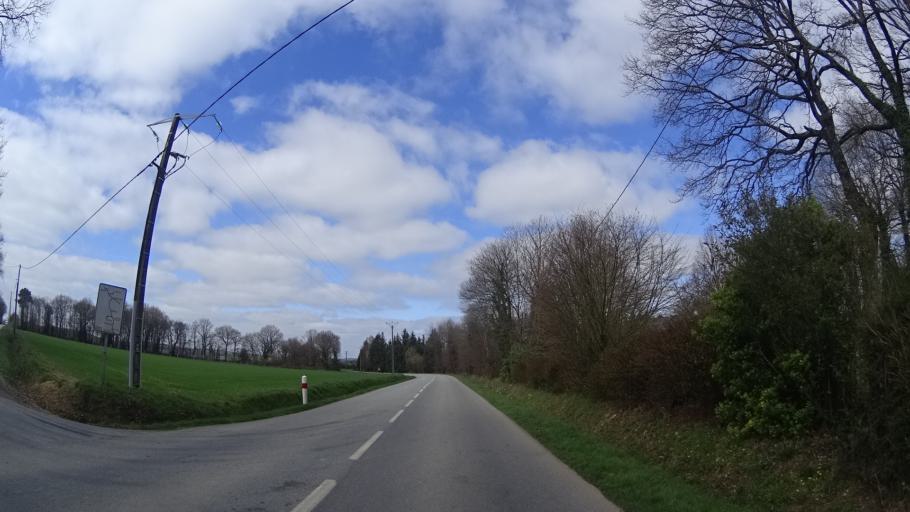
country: FR
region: Brittany
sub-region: Departement du Morbihan
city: Ruffiac
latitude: 47.8242
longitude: -2.2902
